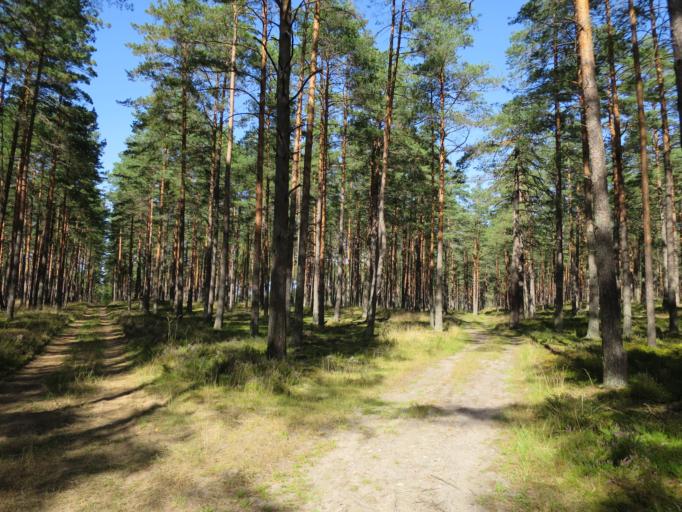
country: LV
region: Riga
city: Jaunciems
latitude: 57.0548
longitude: 24.2199
